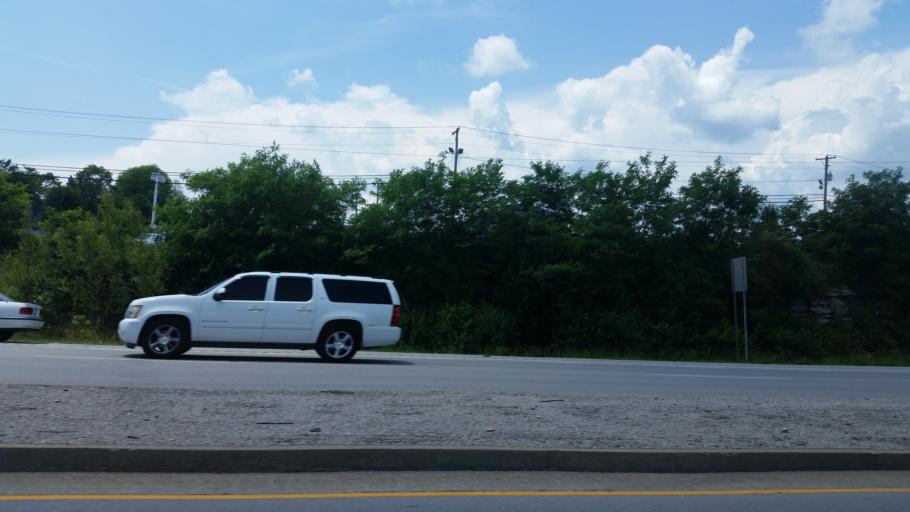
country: US
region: Kentucky
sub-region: Franklin County
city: Frankfort
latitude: 38.1528
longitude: -84.8946
